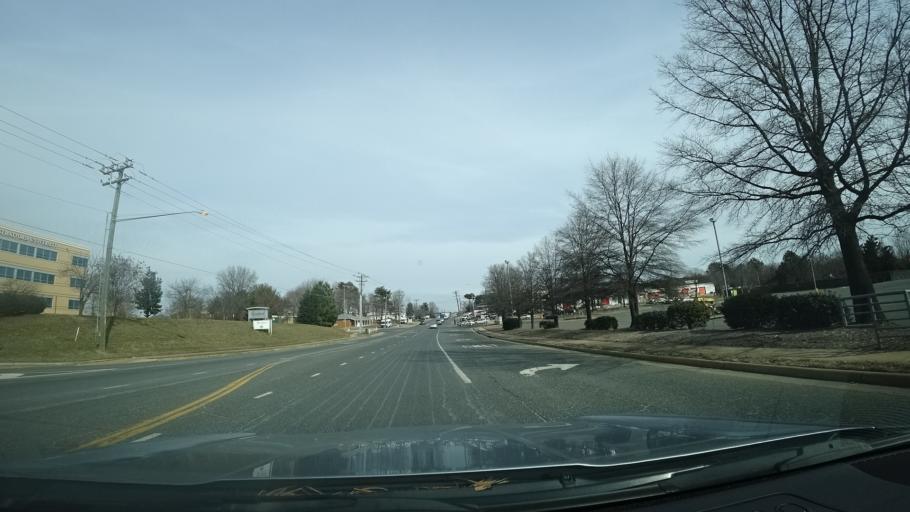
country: US
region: Virginia
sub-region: Prince William County
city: Potomac Mills
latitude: 38.6378
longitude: -77.2918
